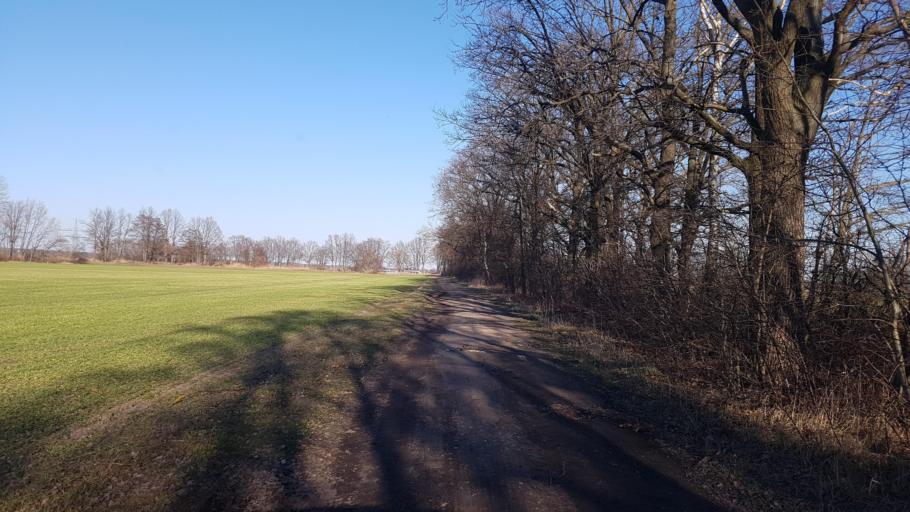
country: DE
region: Brandenburg
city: Plessa
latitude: 51.4444
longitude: 13.6153
